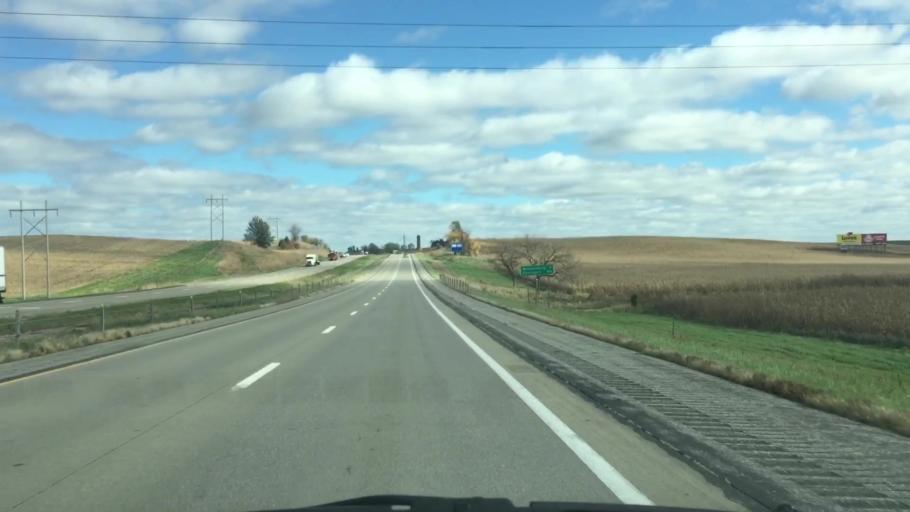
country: US
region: Iowa
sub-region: Iowa County
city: Williamsburg
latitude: 41.6878
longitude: -92.0561
